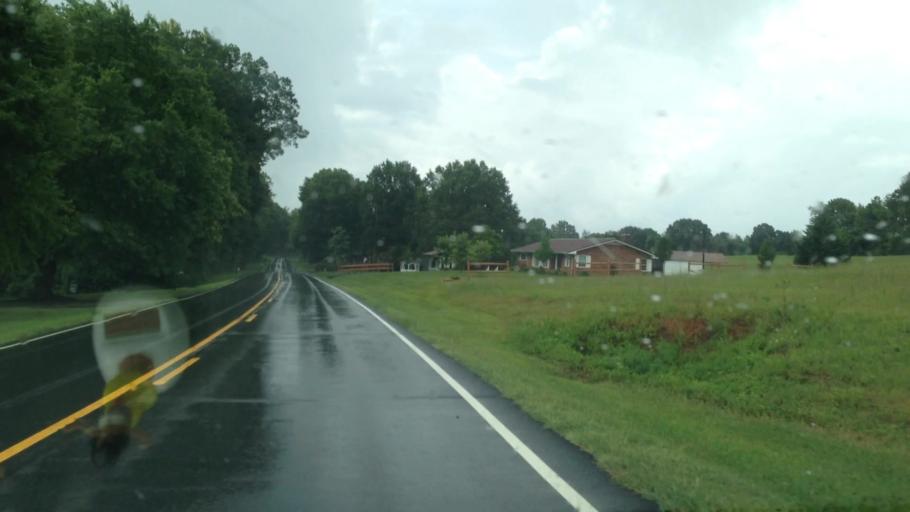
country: US
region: North Carolina
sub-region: Stokes County
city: Danbury
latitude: 36.4453
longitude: -80.1051
